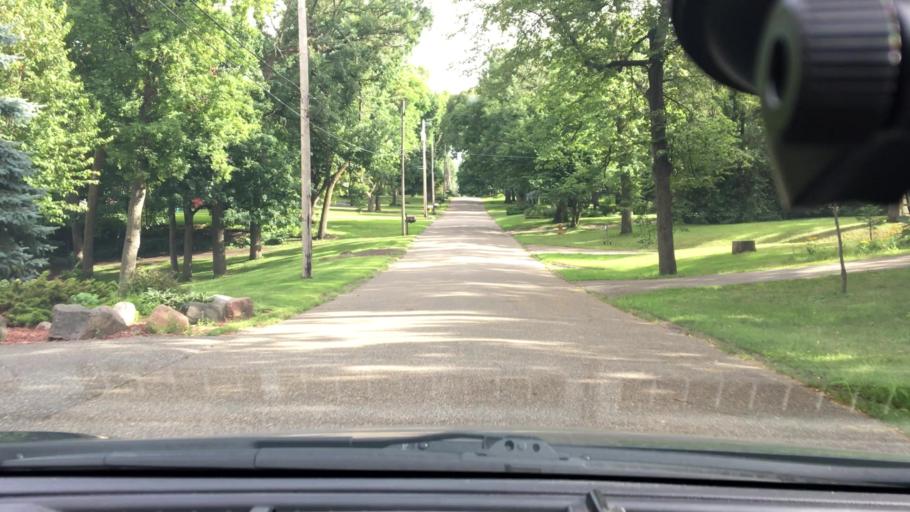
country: US
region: Minnesota
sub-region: Hennepin County
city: Plymouth
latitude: 45.0036
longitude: -93.4400
